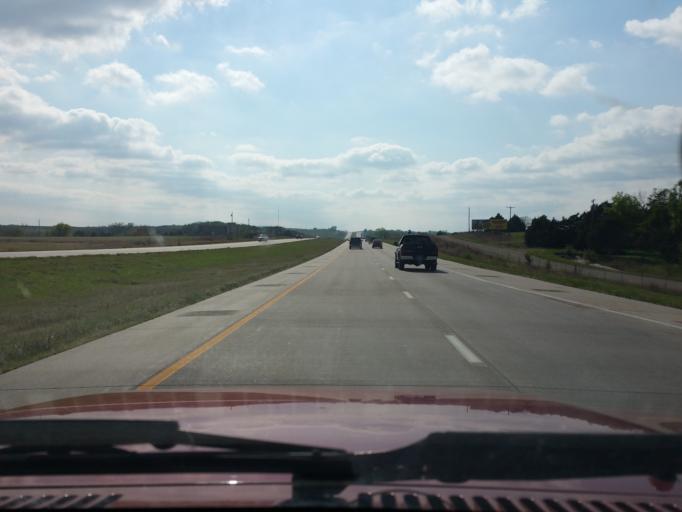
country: US
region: Kansas
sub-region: Wabaunsee County
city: Alma
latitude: 39.0655
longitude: -96.2571
